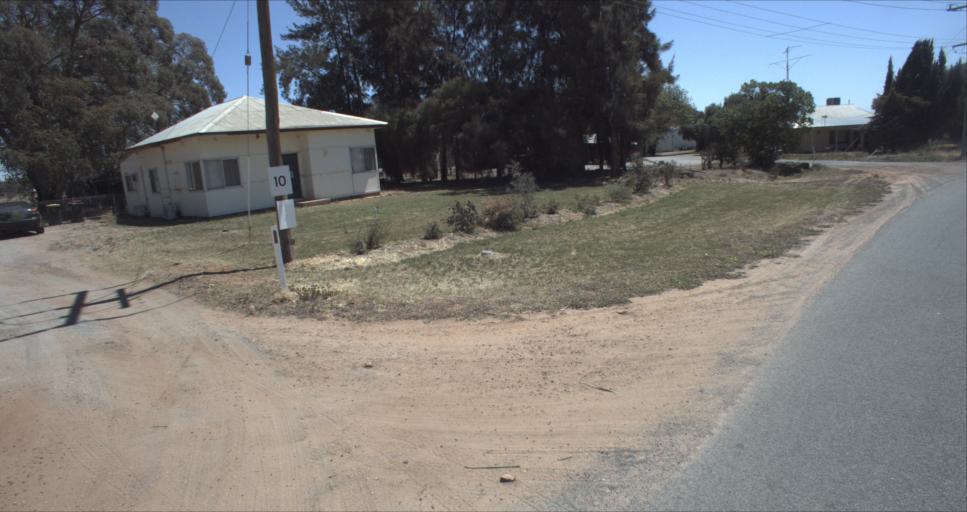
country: AU
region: New South Wales
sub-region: Leeton
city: Leeton
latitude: -34.5378
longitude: 146.3956
